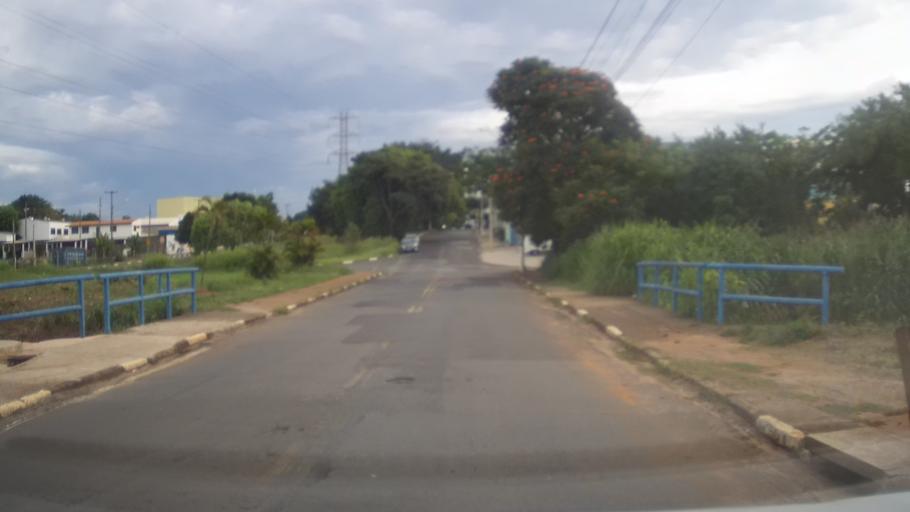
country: BR
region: Sao Paulo
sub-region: Campinas
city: Campinas
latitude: -22.8809
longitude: -47.1253
